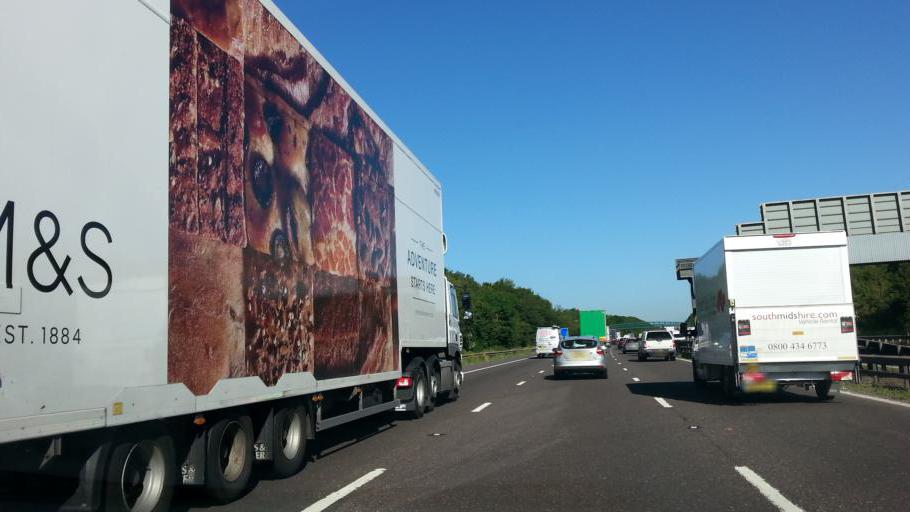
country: GB
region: England
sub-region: Warwickshire
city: Exhall
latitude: 52.4406
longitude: -1.4424
